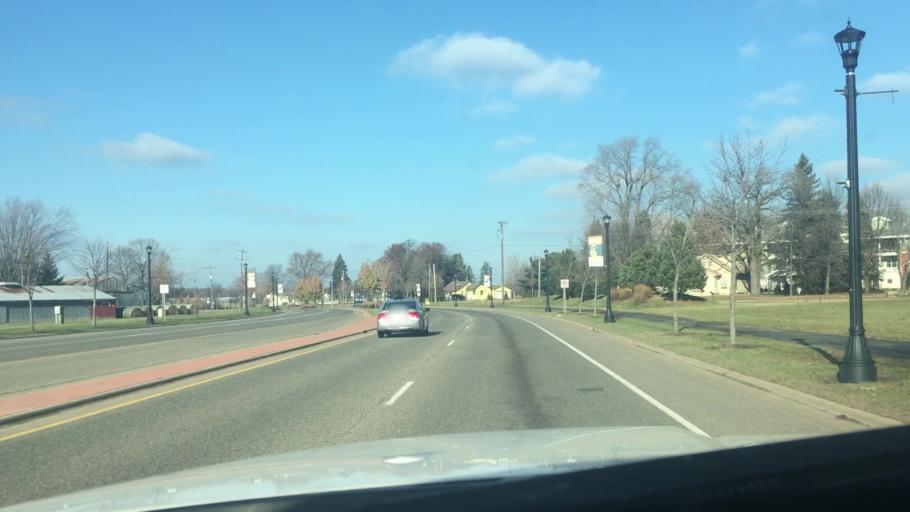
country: US
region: Minnesota
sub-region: Washington County
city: Hugo
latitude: 45.1589
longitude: -92.9983
